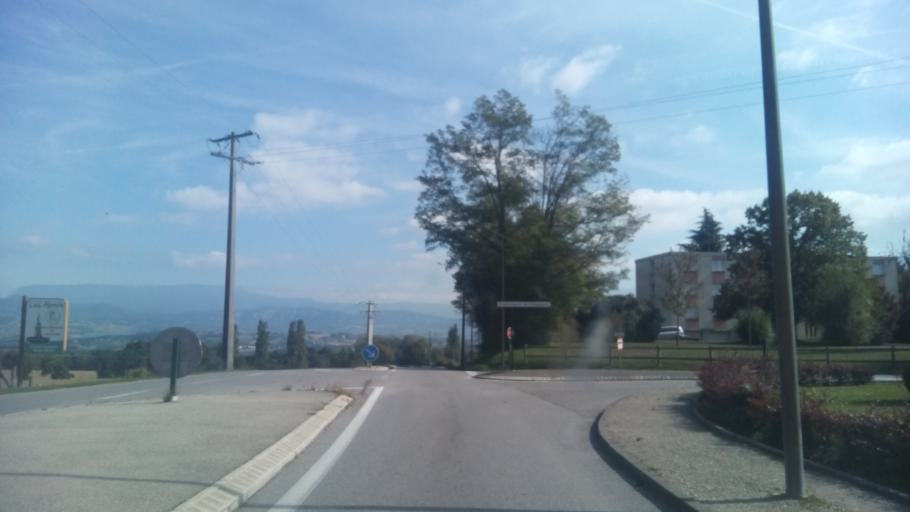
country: FR
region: Rhone-Alpes
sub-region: Departement de l'Isere
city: Les Abrets
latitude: 45.5373
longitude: 5.5916
